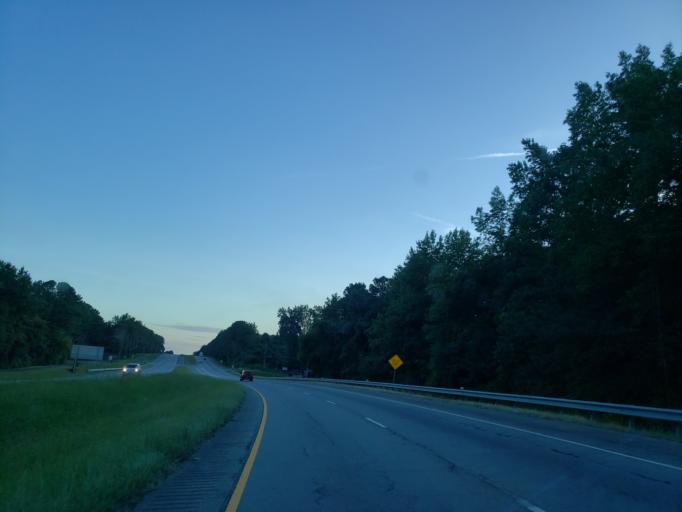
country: US
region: Georgia
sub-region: Floyd County
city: Lindale
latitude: 34.2133
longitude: -85.1884
